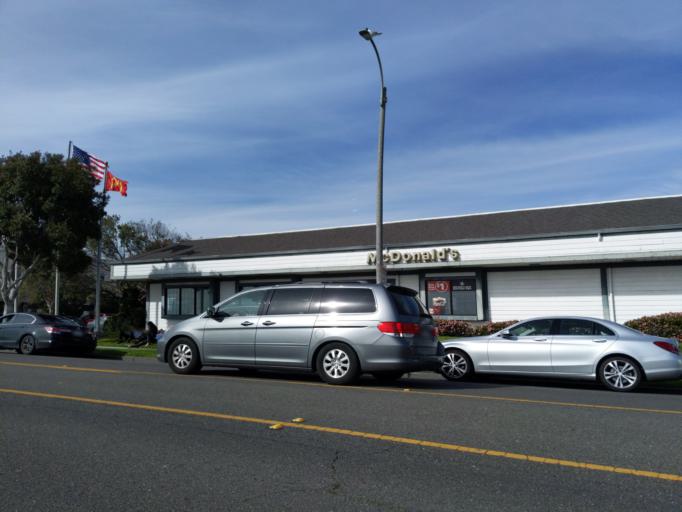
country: US
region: California
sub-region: Alameda County
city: Alameda
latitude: 37.7550
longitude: -122.2521
